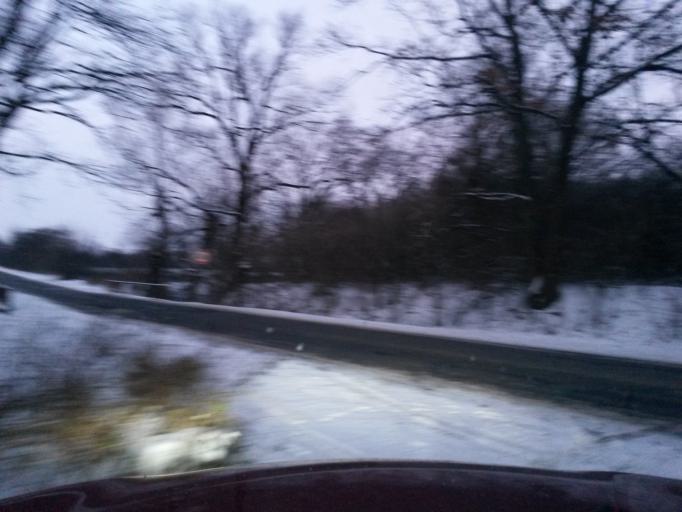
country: SK
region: Kosicky
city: Kosice
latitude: 48.7365
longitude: 21.3262
